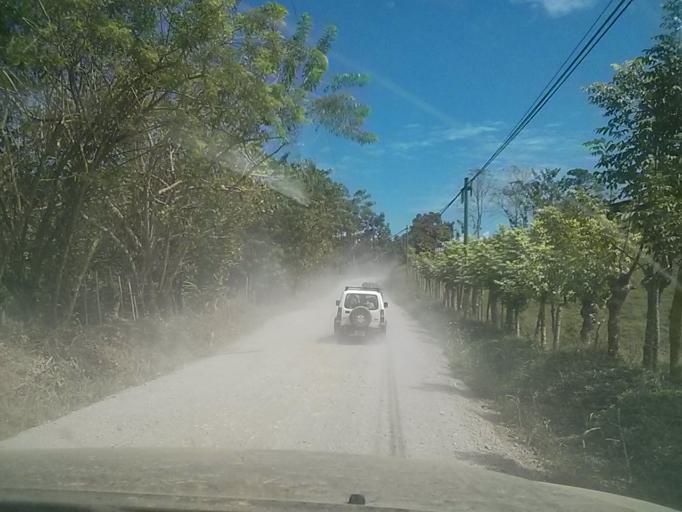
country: CR
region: Puntarenas
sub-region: Canton de Golfito
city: Golfito
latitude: 8.4543
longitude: -83.0549
